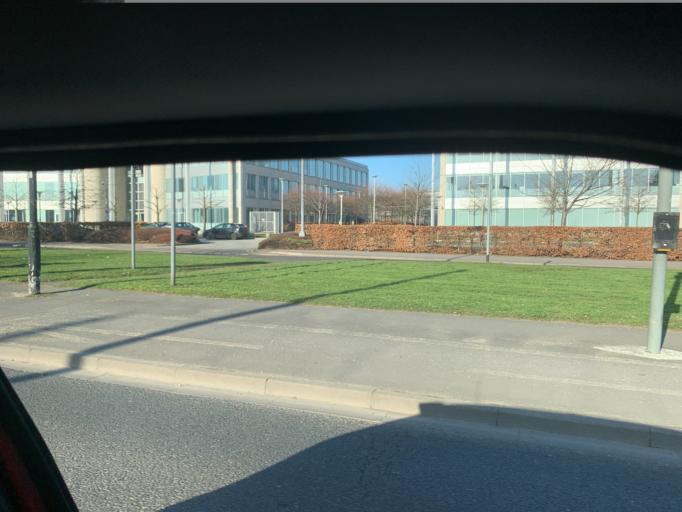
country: GB
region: England
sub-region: Slough
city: Slough
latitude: 51.5146
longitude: -0.6202
